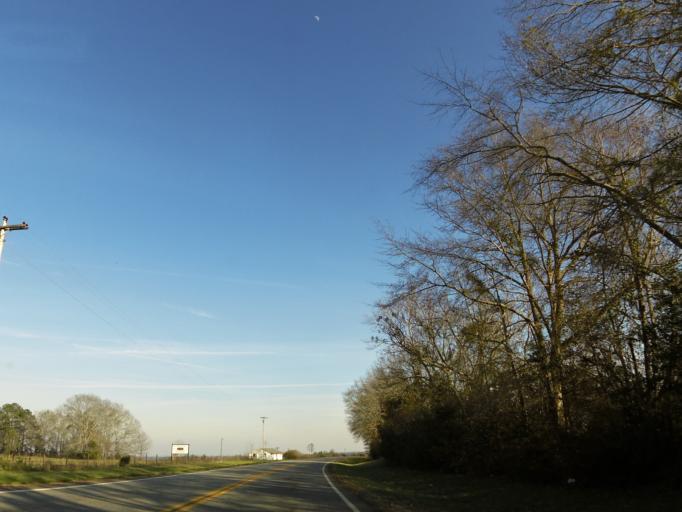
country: US
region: Georgia
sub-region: Stewart County
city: Richland
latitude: 32.1077
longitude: -84.6215
